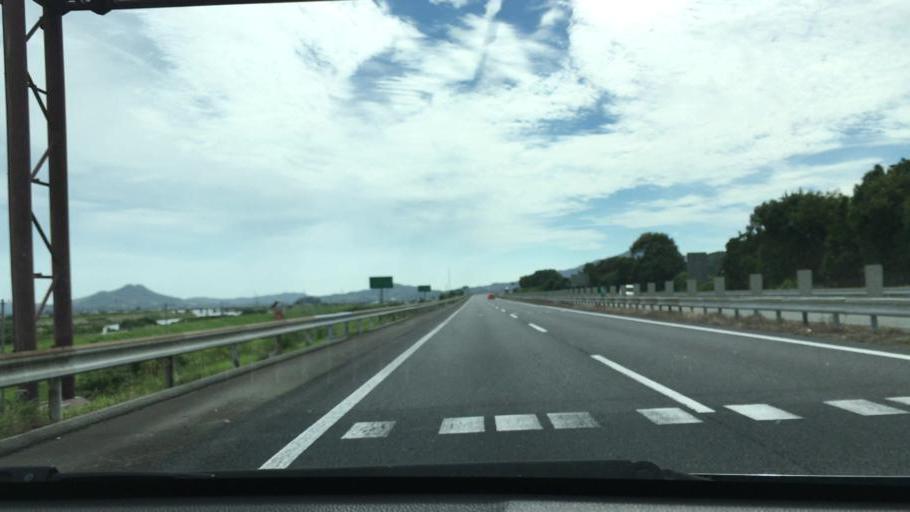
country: JP
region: Yamaguchi
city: Hofu
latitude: 34.0533
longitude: 131.5296
